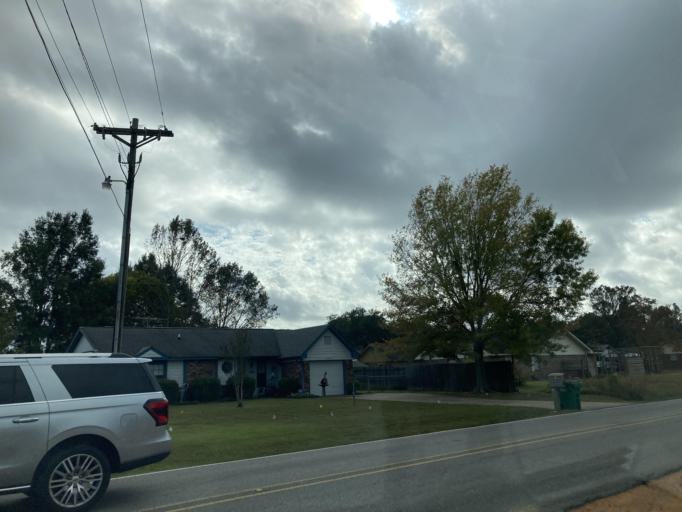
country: US
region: Mississippi
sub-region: Jackson County
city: Gulf Hills
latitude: 30.4390
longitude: -88.8183
